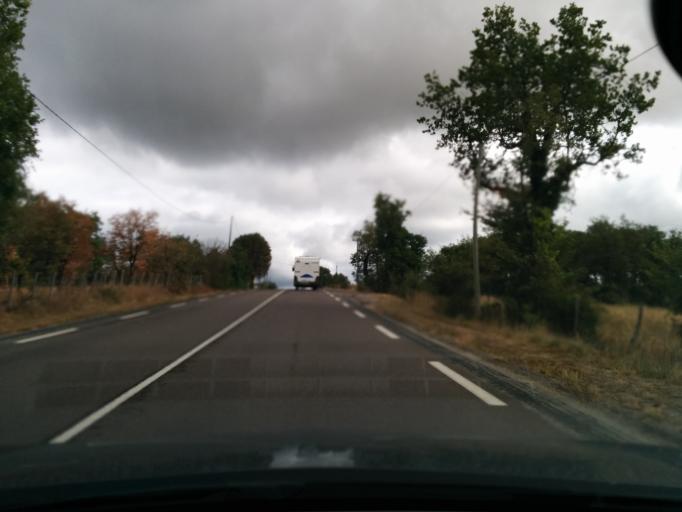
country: FR
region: Midi-Pyrenees
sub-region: Departement du Lot
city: Souillac
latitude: 44.9992
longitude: 1.5146
